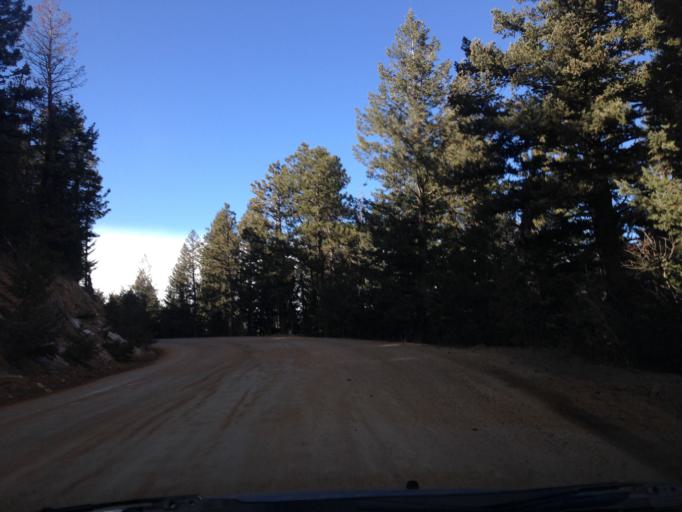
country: US
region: Colorado
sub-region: Boulder County
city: Coal Creek
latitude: 39.9208
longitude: -105.3461
